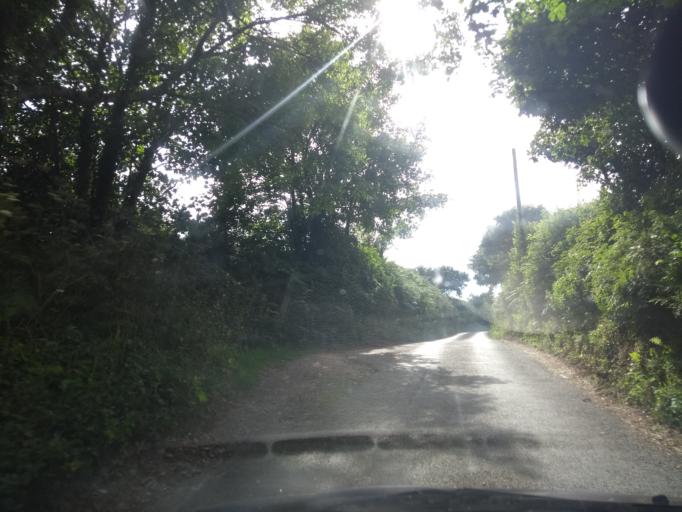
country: GB
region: England
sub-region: Devon
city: Modbury
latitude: 50.3064
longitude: -3.8618
